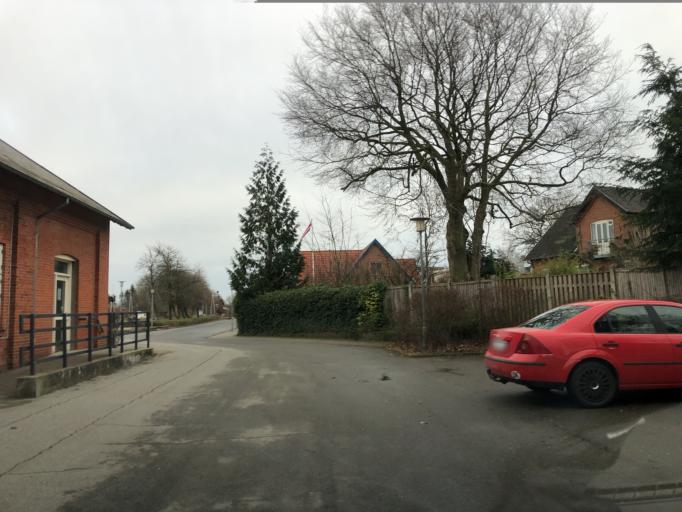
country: DK
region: Central Jutland
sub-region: Viborg Kommune
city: Stoholm
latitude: 56.4873
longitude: 9.1499
